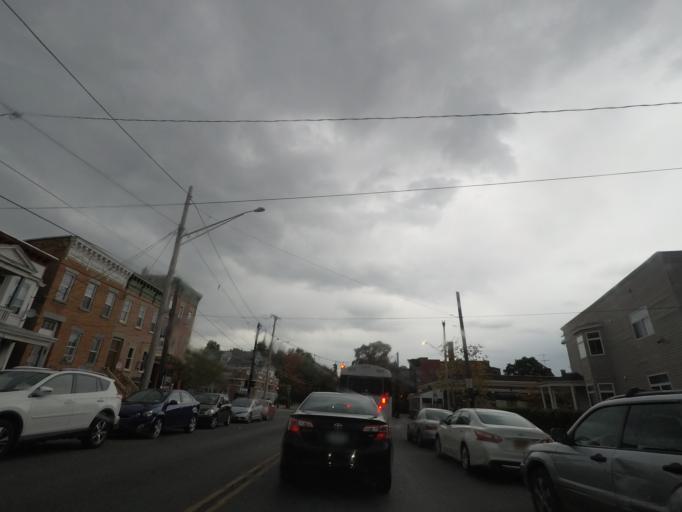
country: US
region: New York
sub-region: Albany County
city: West Albany
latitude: 42.6621
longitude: -73.7778
